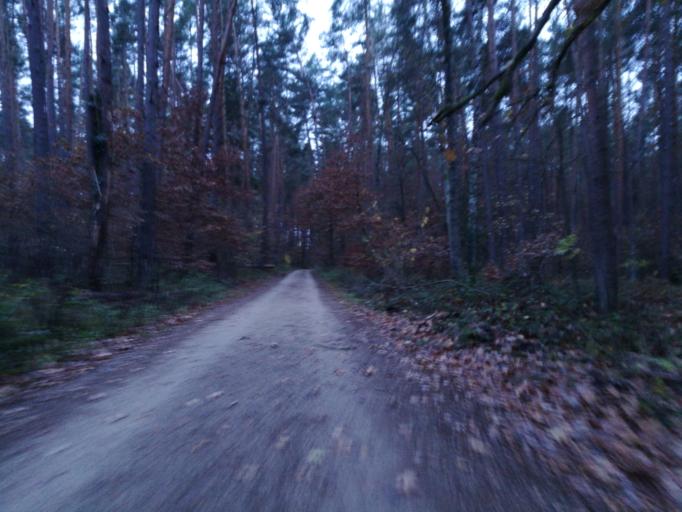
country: DE
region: Bavaria
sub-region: Regierungsbezirk Mittelfranken
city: Seukendorf
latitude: 49.4720
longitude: 10.8919
